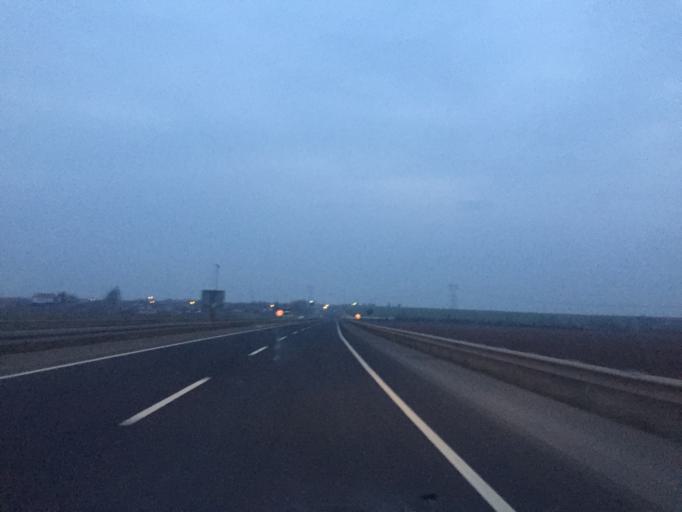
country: TR
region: Sanliurfa
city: Camlidere
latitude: 37.1599
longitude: 39.0276
